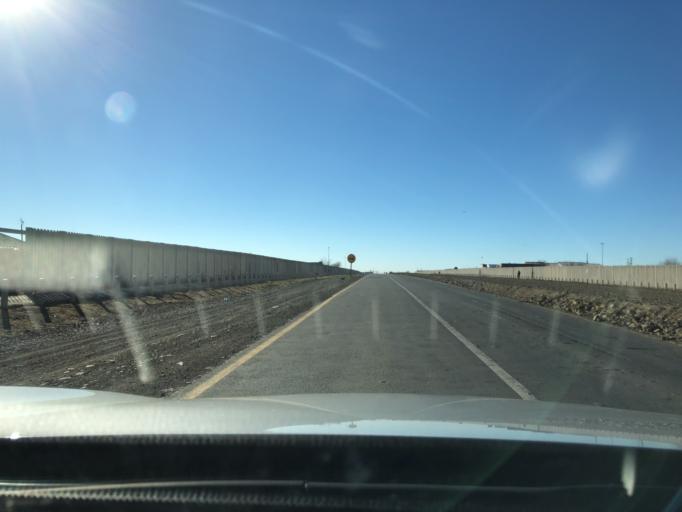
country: ZA
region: Mpumalanga
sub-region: Gert Sibande District Municipality
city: Standerton
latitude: -26.9400
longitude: 29.2027
